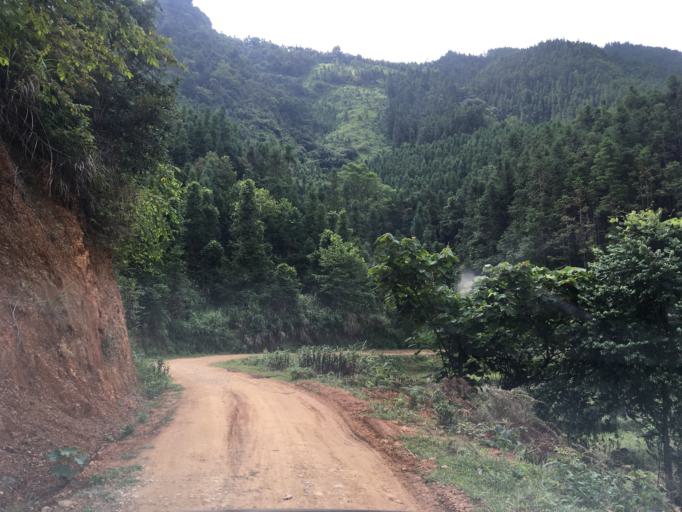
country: CN
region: Guangxi Zhuangzu Zizhiqu
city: Xinzhou
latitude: 24.8808
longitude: 105.8453
